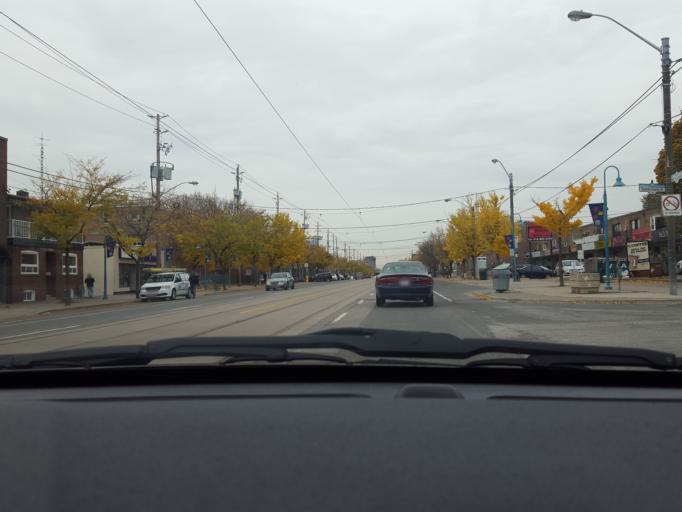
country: CA
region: Ontario
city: Etobicoke
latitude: 43.5971
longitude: -79.5224
